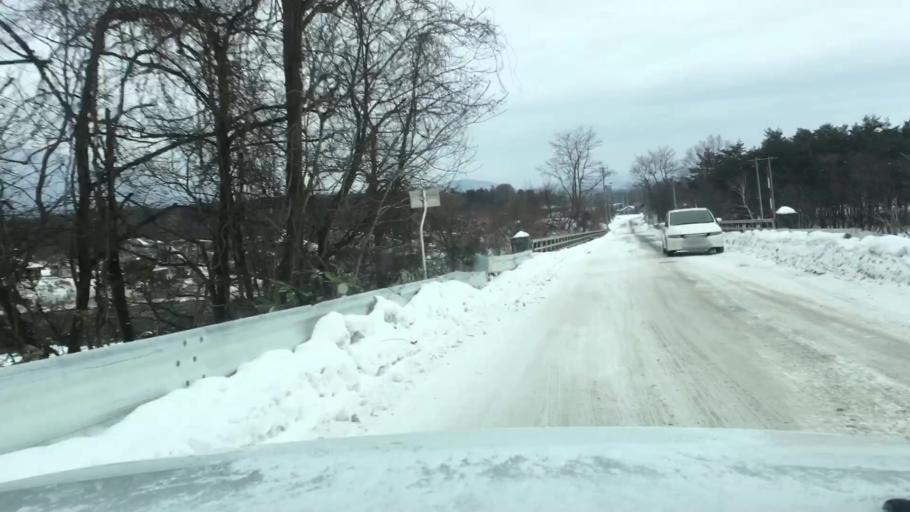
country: JP
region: Iwate
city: Shizukuishi
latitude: 39.9116
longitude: 141.0048
